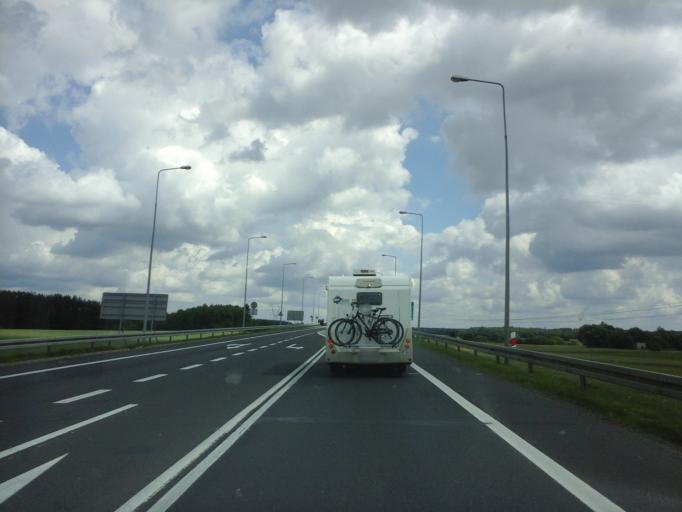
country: PL
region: West Pomeranian Voivodeship
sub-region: Powiat bialogardzki
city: Karlino
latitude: 54.0314
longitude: 15.8927
